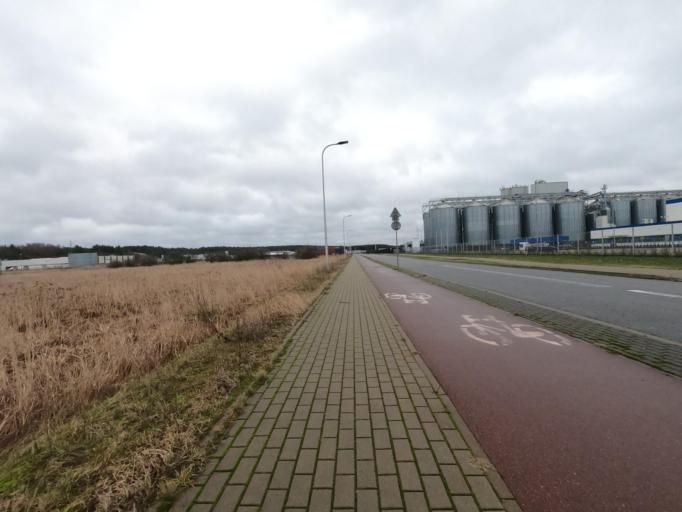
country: PL
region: Greater Poland Voivodeship
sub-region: Powiat pilski
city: Pila
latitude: 53.1416
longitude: 16.7746
